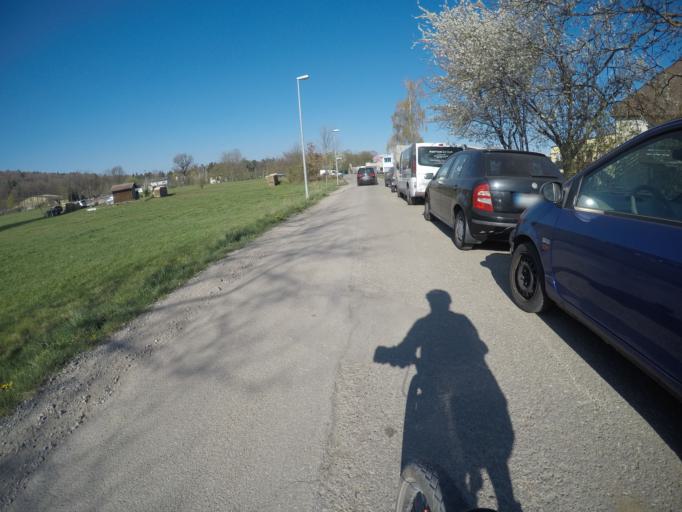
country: DE
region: Baden-Wuerttemberg
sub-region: Tuebingen Region
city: Dettenhausen
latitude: 48.6002
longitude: 9.1018
